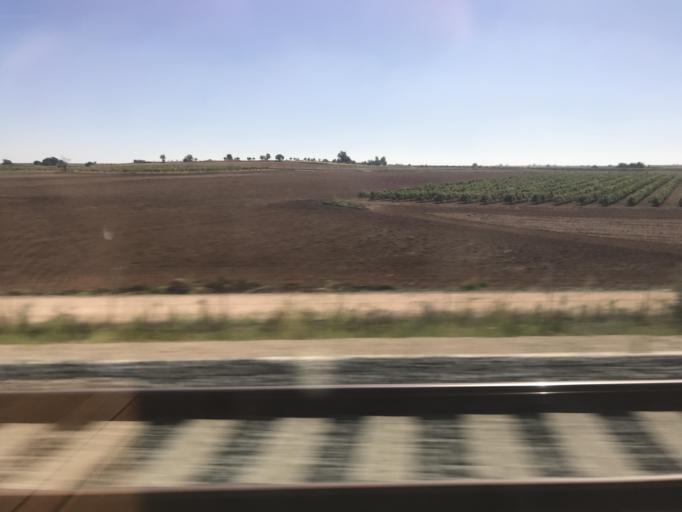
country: ES
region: Castille-La Mancha
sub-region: Provincia de Cuenca
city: Zarza de Tajo
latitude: 39.9789
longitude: -3.1459
